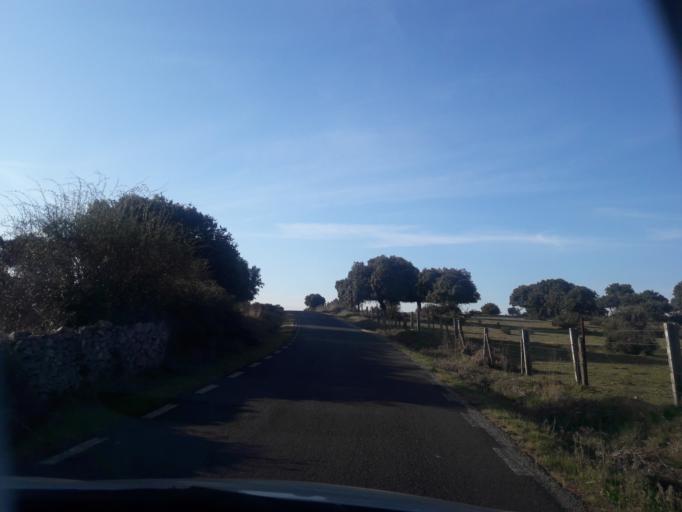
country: ES
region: Castille and Leon
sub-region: Provincia de Salamanca
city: Montejo
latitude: 40.6193
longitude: -5.6082
